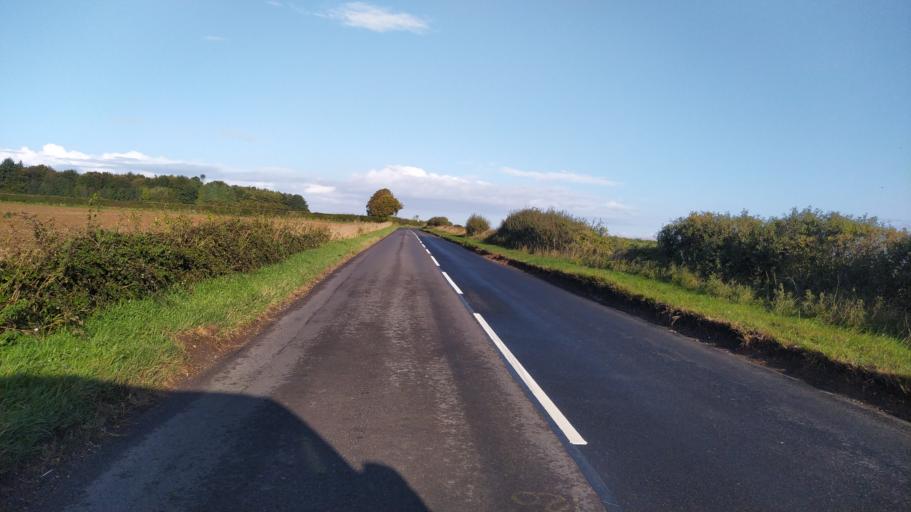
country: GB
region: England
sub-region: Dorset
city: Wimborne Minster
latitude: 50.8872
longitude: -2.0004
